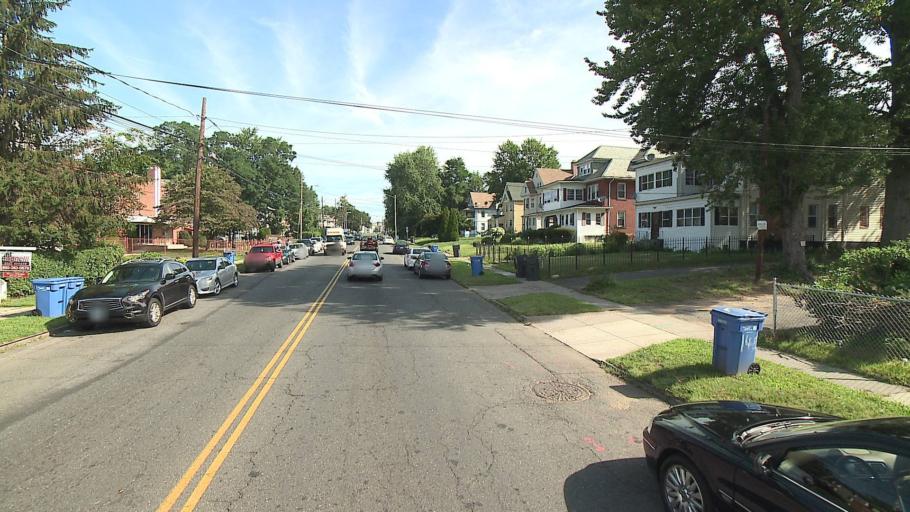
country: US
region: Connecticut
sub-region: Hartford County
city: Blue Hills
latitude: 41.7880
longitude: -72.6985
